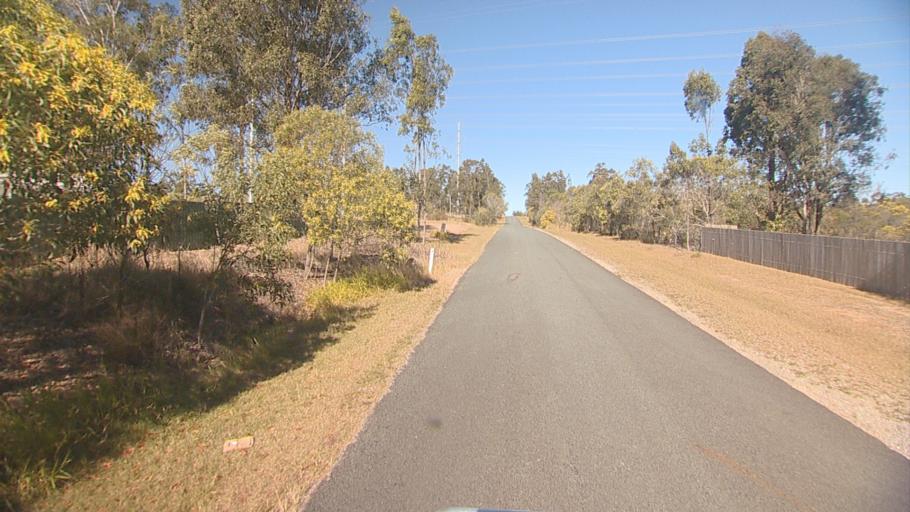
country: AU
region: Queensland
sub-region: Ipswich
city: Springfield Lakes
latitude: -27.7173
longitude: 152.9304
